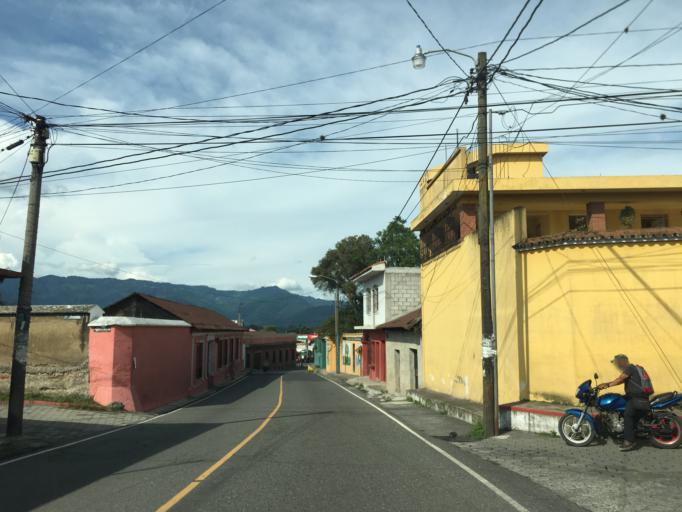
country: GT
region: Sacatepequez
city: Ciudad Vieja
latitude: 14.5245
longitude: -90.7667
